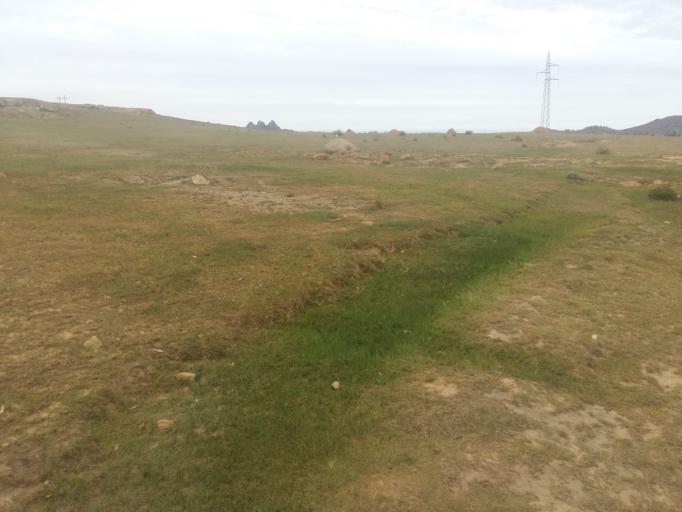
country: LS
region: Mafeteng
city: Mafeteng
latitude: -29.6916
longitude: 27.4302
